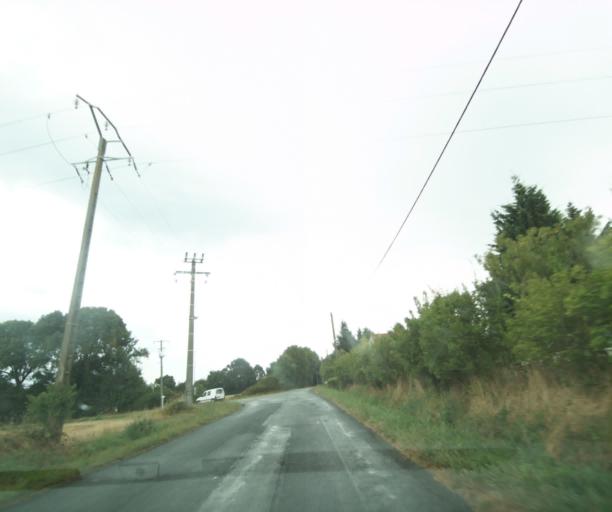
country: FR
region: Poitou-Charentes
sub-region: Departement de la Charente-Maritime
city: Tonnay-Charente
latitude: 45.9407
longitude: -0.8739
